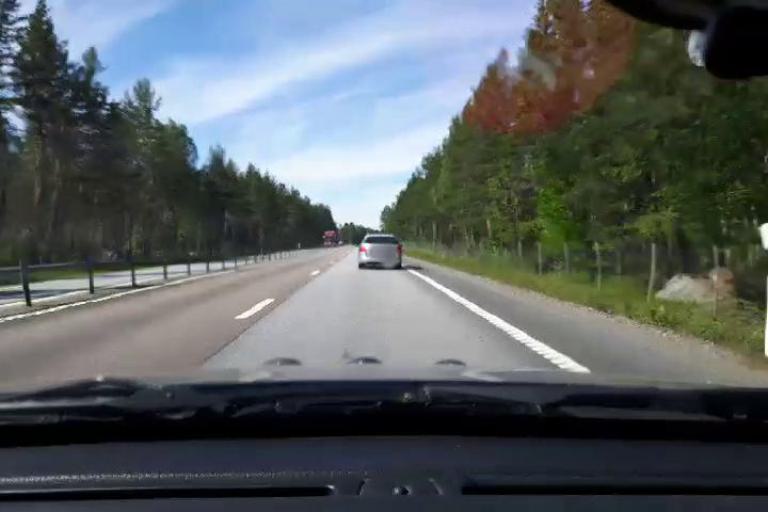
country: SE
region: Gaevleborg
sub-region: Gavle Kommun
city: Norrsundet
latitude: 60.9660
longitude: 17.0293
